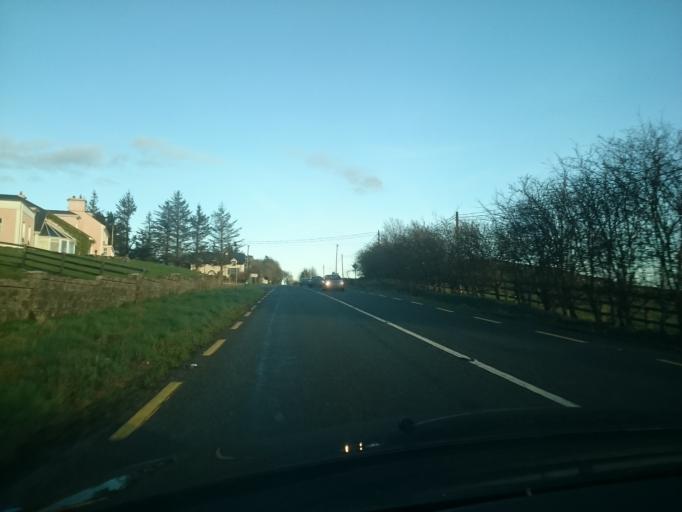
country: IE
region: Connaught
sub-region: Maigh Eo
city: Claremorris
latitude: 53.7747
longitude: -9.0673
